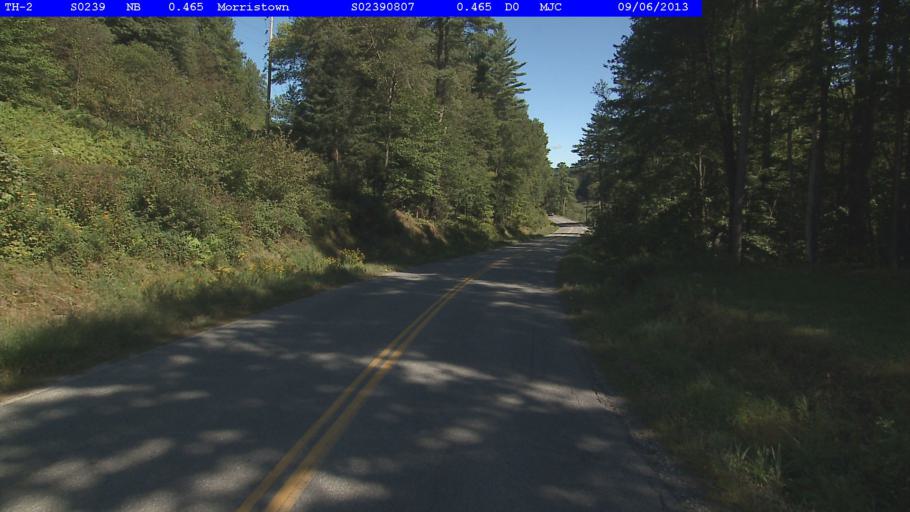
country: US
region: Vermont
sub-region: Lamoille County
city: Morristown
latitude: 44.5608
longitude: -72.6153
